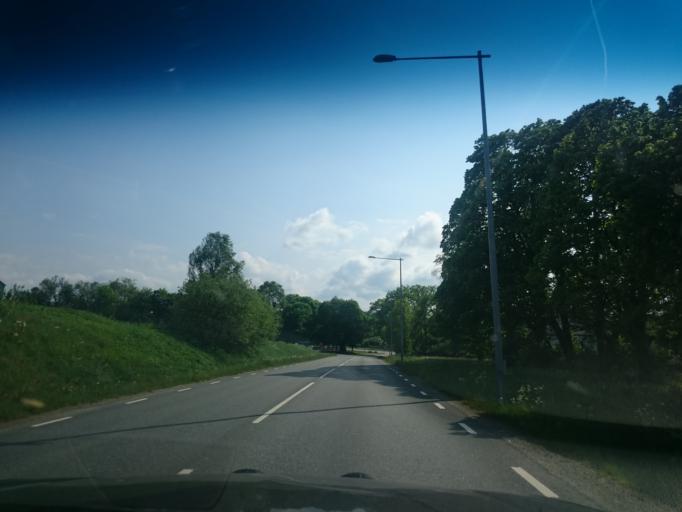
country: SE
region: Joenkoeping
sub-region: Vetlanda Kommun
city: Landsbro
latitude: 57.3846
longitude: 14.9603
